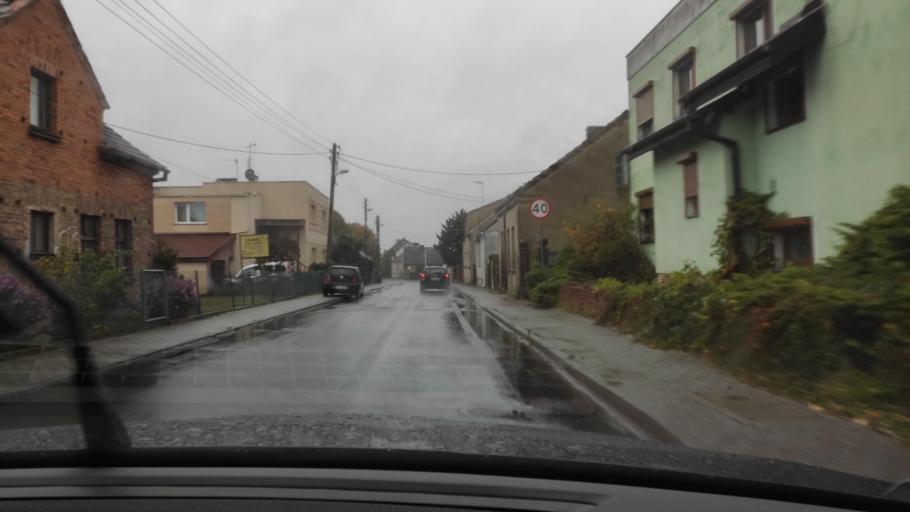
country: PL
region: Greater Poland Voivodeship
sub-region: Powiat poznanski
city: Kornik
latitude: 52.2246
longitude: 17.0959
